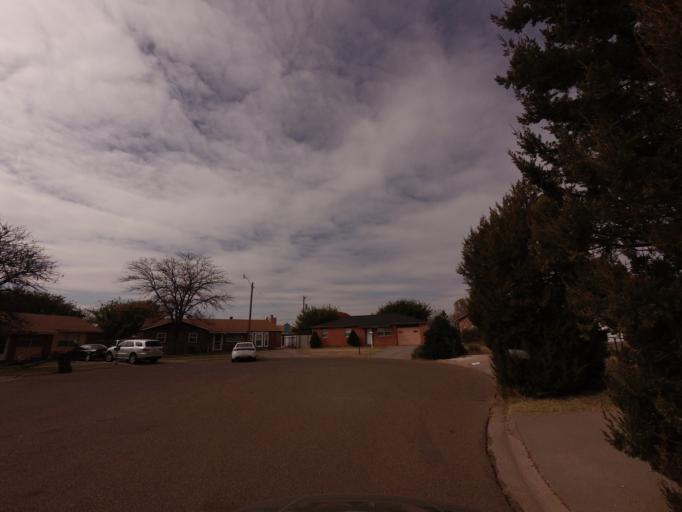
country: US
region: New Mexico
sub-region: Curry County
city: Clovis
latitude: 34.4284
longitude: -103.2304
